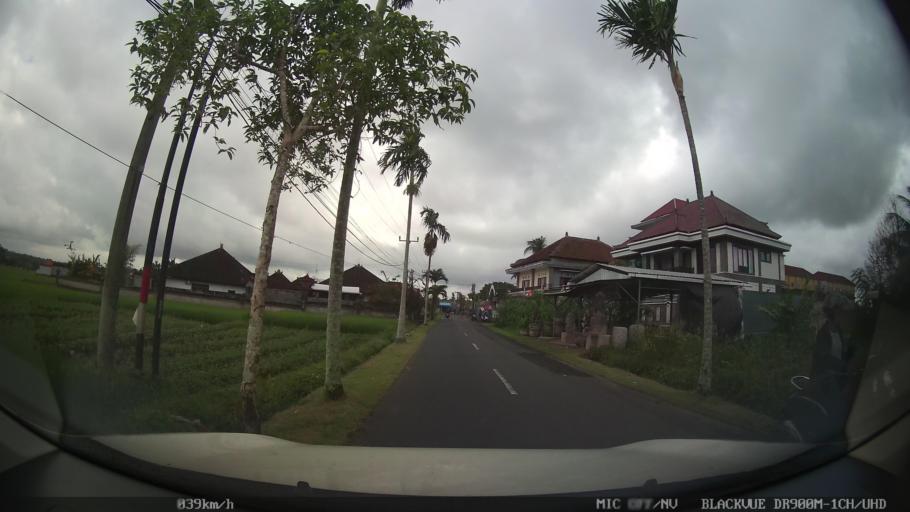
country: ID
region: Bali
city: Banjar Mambalkajanan
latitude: -8.5472
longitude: 115.2127
